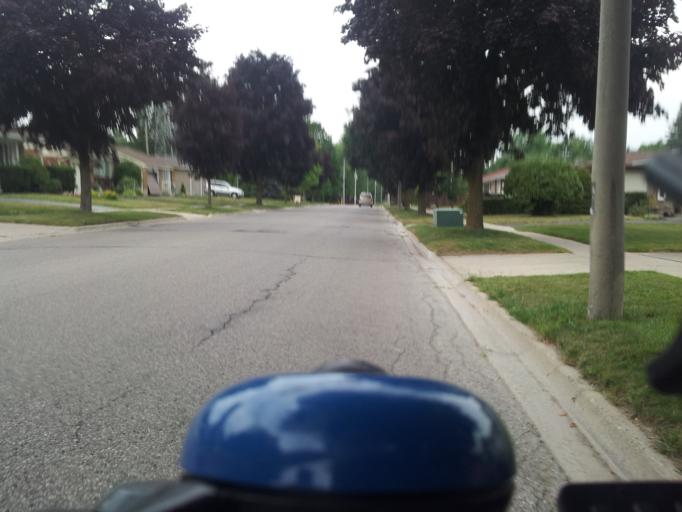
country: CA
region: Ontario
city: Stratford
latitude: 43.3748
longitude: -80.9540
